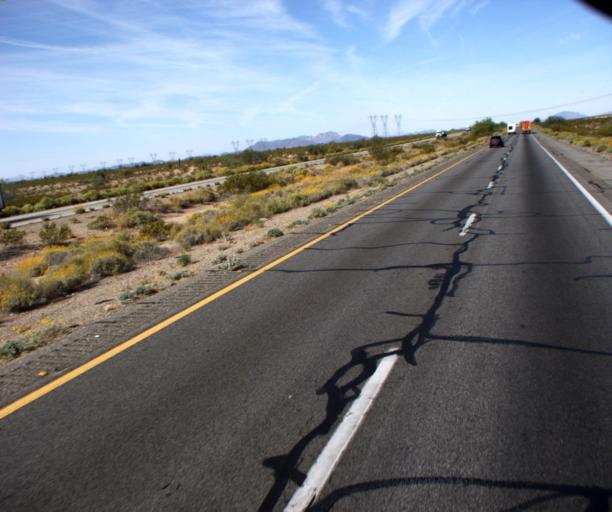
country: US
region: Arizona
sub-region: Maricopa County
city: Buckeye
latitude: 33.4508
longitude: -112.7282
